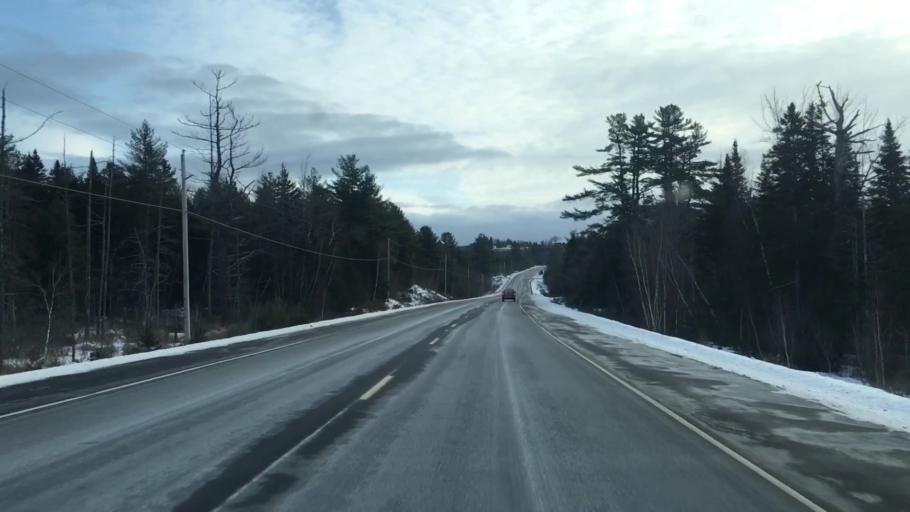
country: US
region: Maine
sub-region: Washington County
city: Machias
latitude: 44.9502
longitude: -67.6828
